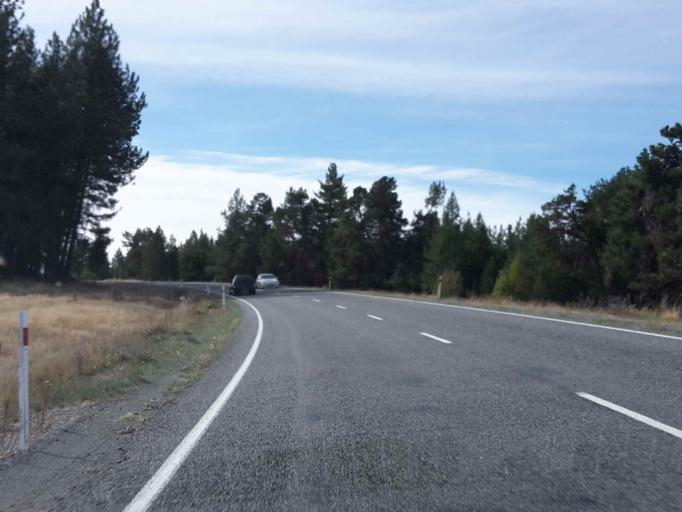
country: NZ
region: Canterbury
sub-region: Timaru District
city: Pleasant Point
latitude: -44.1801
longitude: 170.3185
